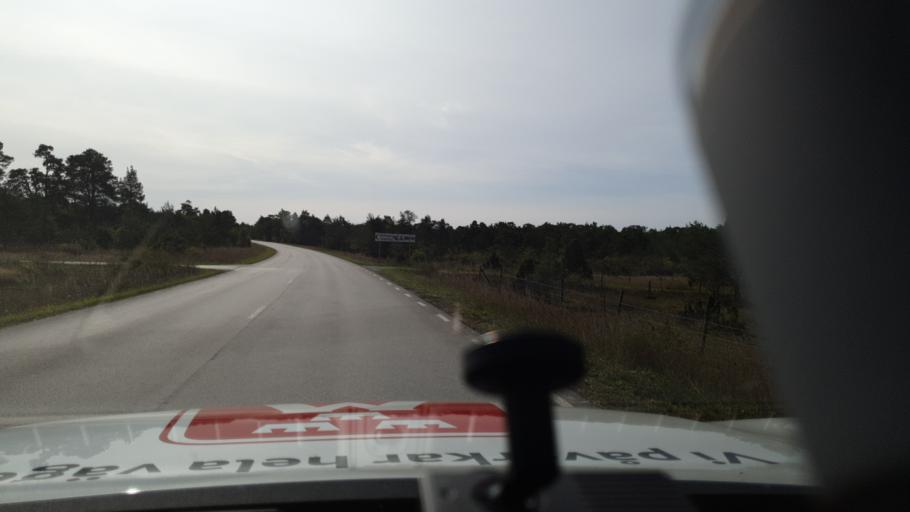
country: SE
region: Gotland
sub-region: Gotland
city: Slite
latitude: 57.8904
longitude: 19.0906
